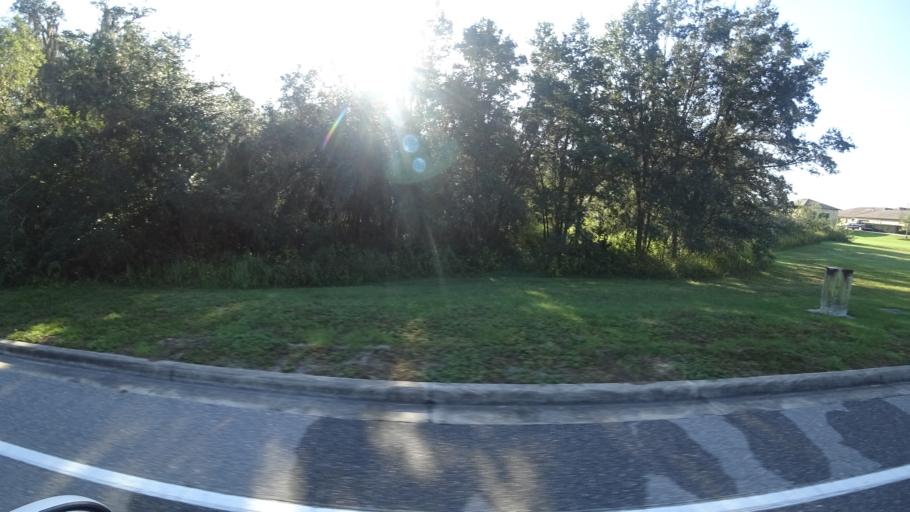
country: US
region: Florida
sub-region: Hillsborough County
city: Sun City Center
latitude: 27.5606
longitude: -82.3568
